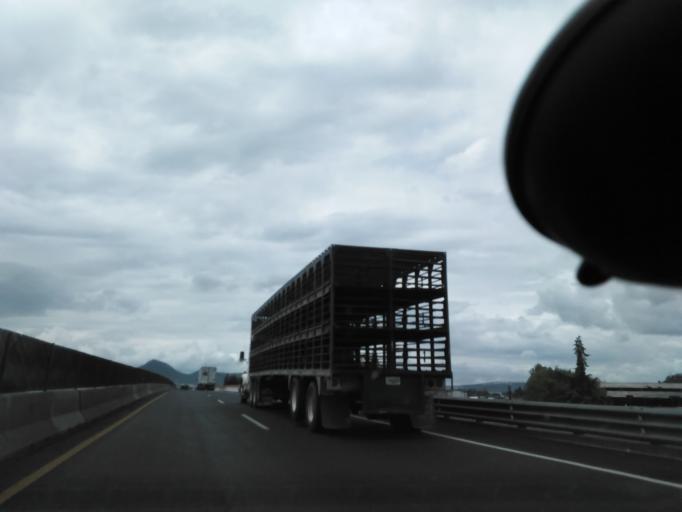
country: MX
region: Morelos
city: San Pedro Xalpa
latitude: 19.8116
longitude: -99.1930
